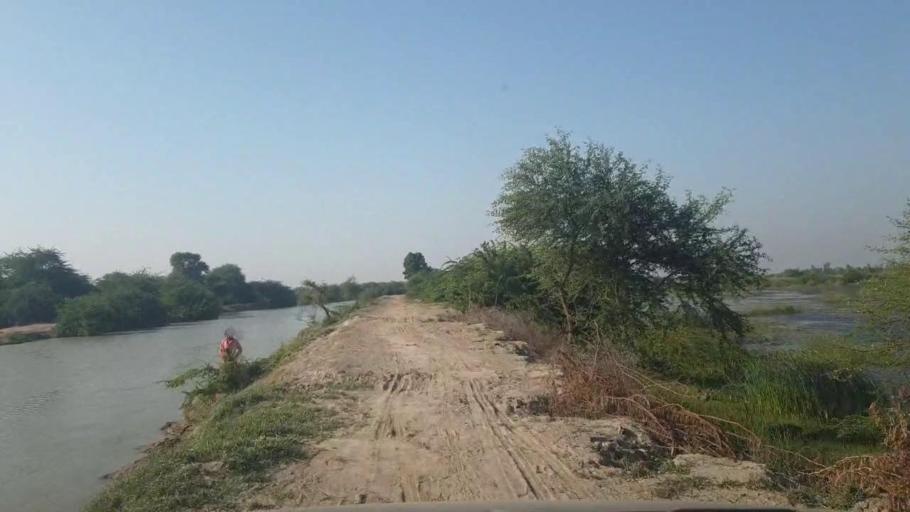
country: PK
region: Sindh
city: Badin
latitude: 24.7109
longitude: 68.8928
